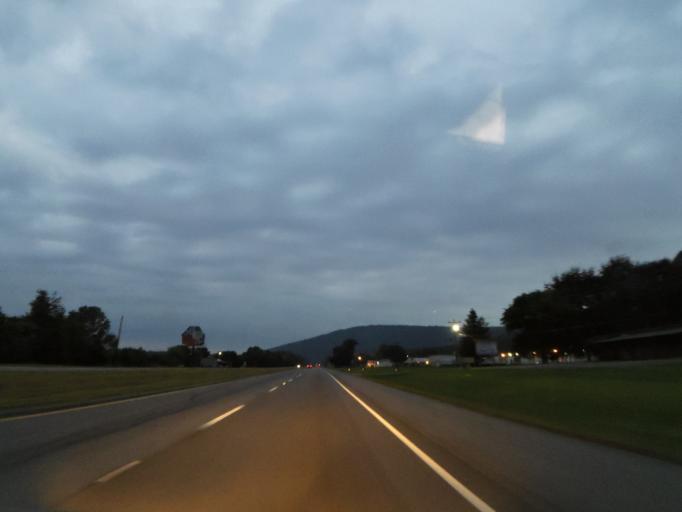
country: US
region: Alabama
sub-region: Madison County
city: New Hope
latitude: 34.6728
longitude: -86.3294
